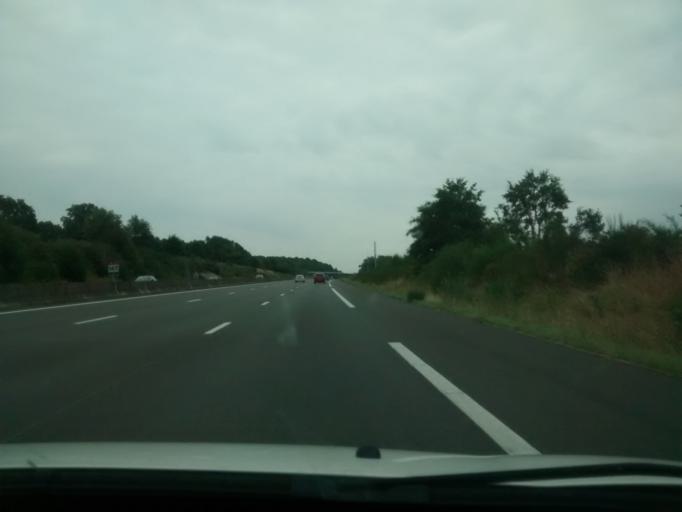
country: FR
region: Pays de la Loire
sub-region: Departement de la Sarthe
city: Connerre
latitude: 48.0828
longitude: 0.4932
